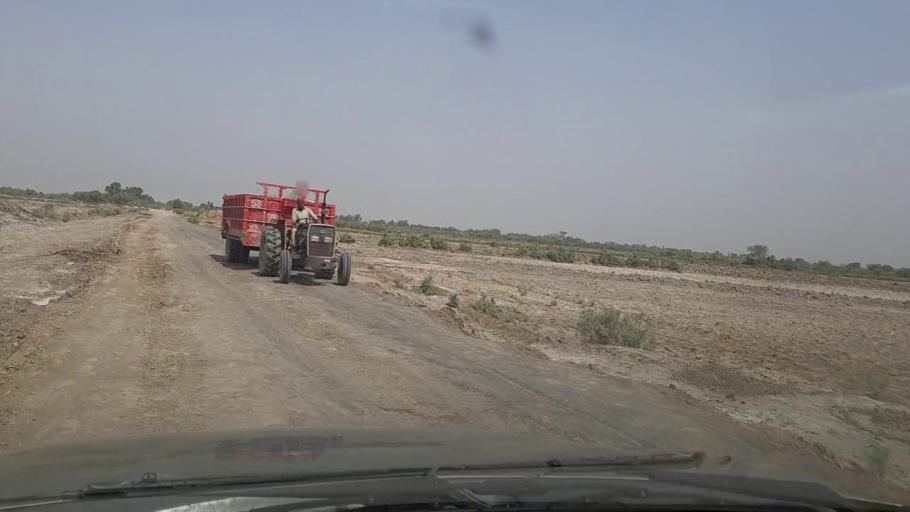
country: PK
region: Sindh
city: Thul
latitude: 28.3968
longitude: 68.7127
